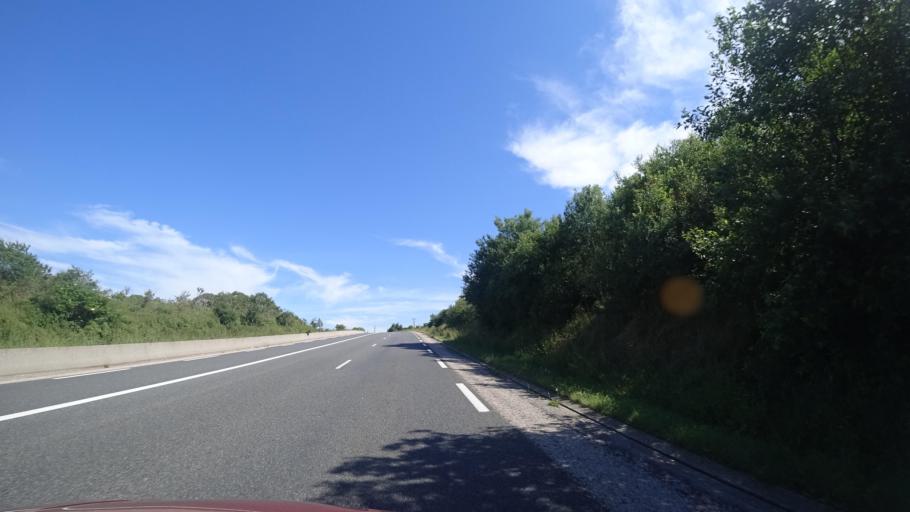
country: FR
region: Midi-Pyrenees
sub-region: Departement de l'Aveyron
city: Pont-de-Salars
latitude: 44.2762
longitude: 2.7242
